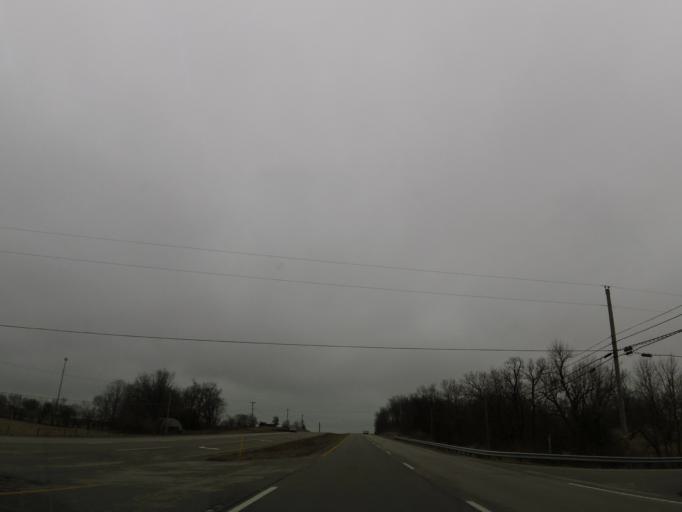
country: US
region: Kentucky
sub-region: Mercer County
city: Jackson
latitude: 37.8242
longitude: -84.8498
